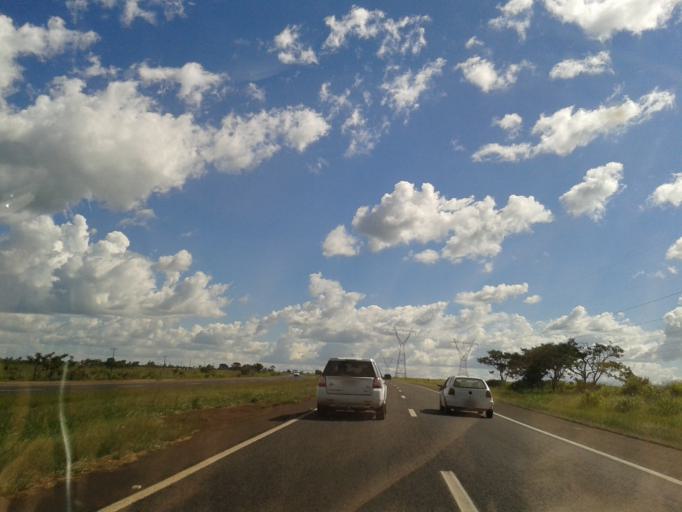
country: BR
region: Goias
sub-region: Goiatuba
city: Goiatuba
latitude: -17.8867
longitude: -49.2327
